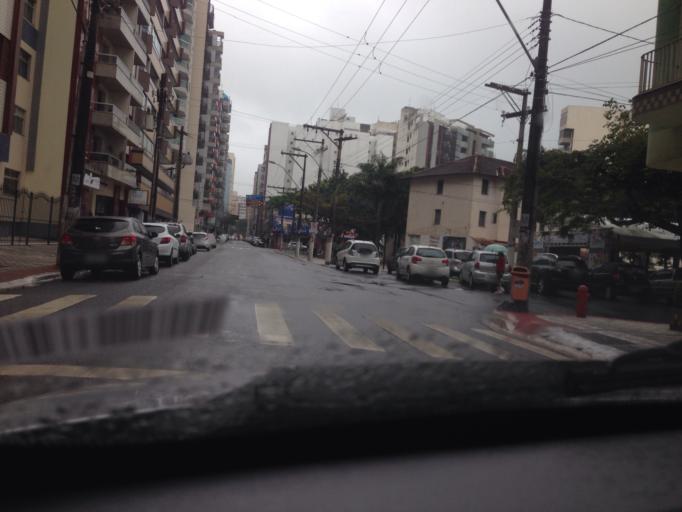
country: BR
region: Espirito Santo
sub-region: Guarapari
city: Guarapari
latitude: -20.6744
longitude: -40.5005
